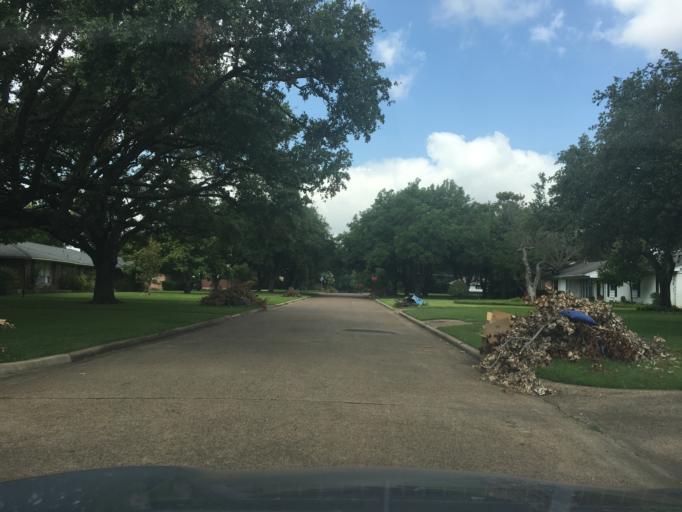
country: US
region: Texas
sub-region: Dallas County
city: Addison
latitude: 32.9132
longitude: -96.8283
